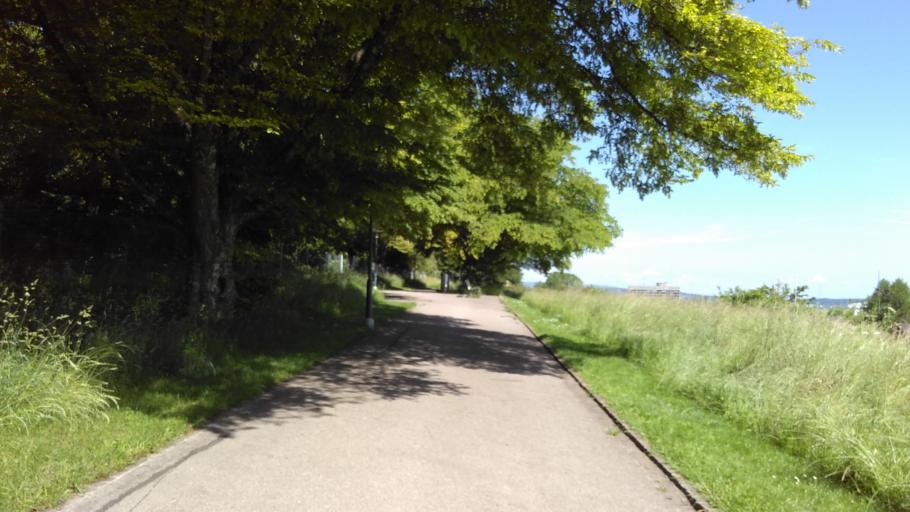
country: CH
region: Zurich
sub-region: Bezirk Zuerich
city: Zuerich (Kreis 3)
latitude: 47.3576
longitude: 8.5023
